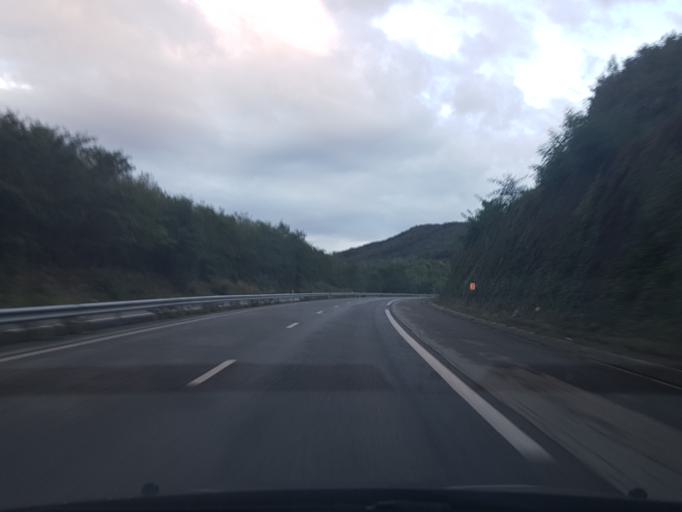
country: FR
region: Midi-Pyrenees
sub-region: Departement de l'Ariege
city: Foix
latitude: 42.9967
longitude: 1.6192
